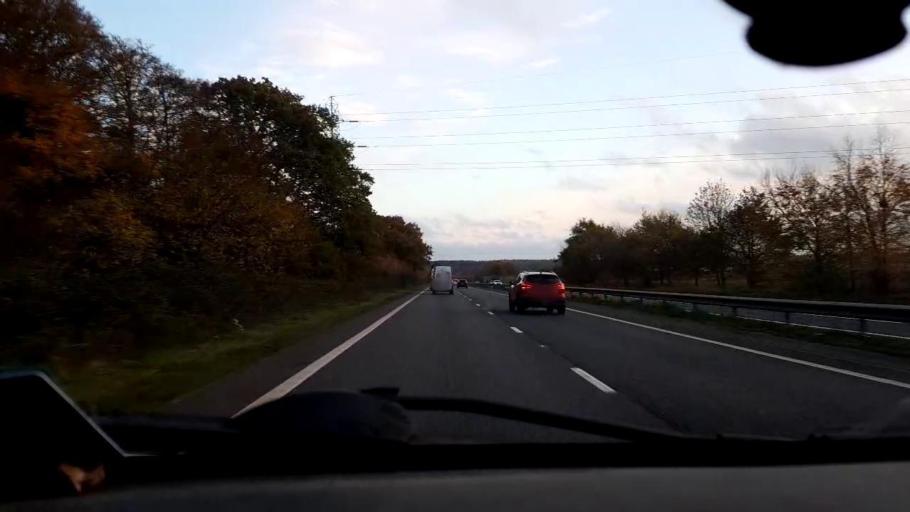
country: GB
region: England
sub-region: Norfolk
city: Costessey
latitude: 52.6424
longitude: 1.1923
